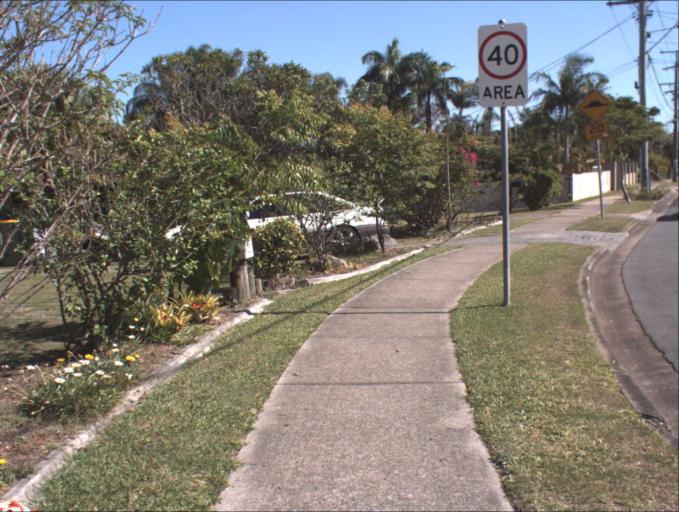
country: AU
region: Queensland
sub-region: Logan
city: Springwood
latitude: -27.6090
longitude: 153.1263
